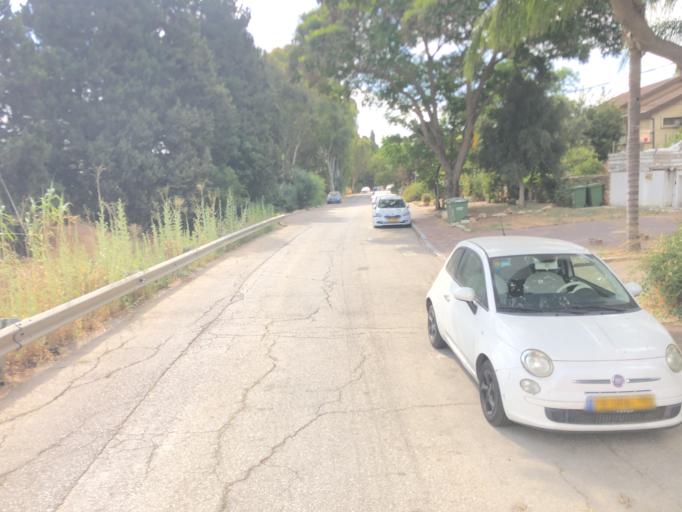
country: IL
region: Central District
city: Yehud
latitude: 32.0409
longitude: 34.8953
